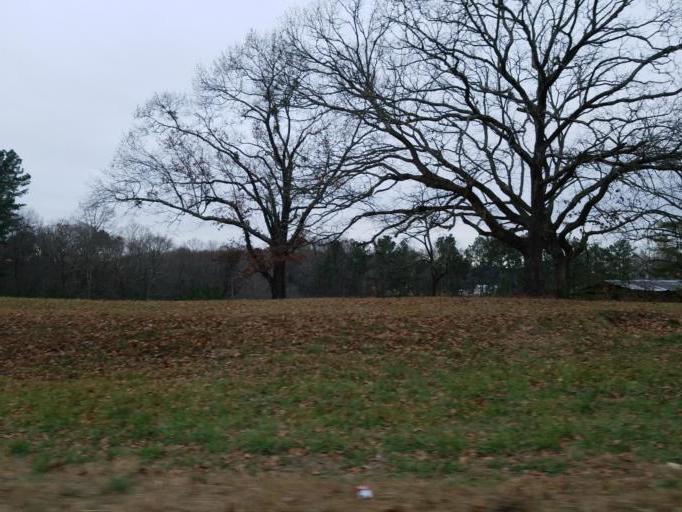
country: US
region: Georgia
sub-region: Dawson County
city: Dawsonville
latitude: 34.4842
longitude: -84.1677
